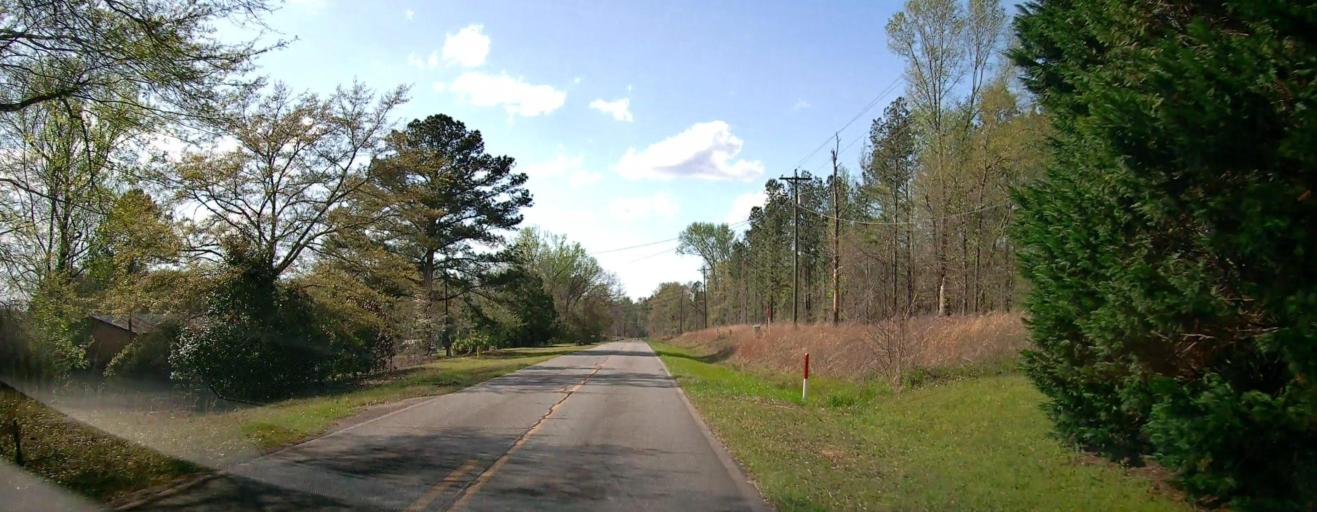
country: US
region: Georgia
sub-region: Baldwin County
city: Hardwick
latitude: 33.0190
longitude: -83.1084
